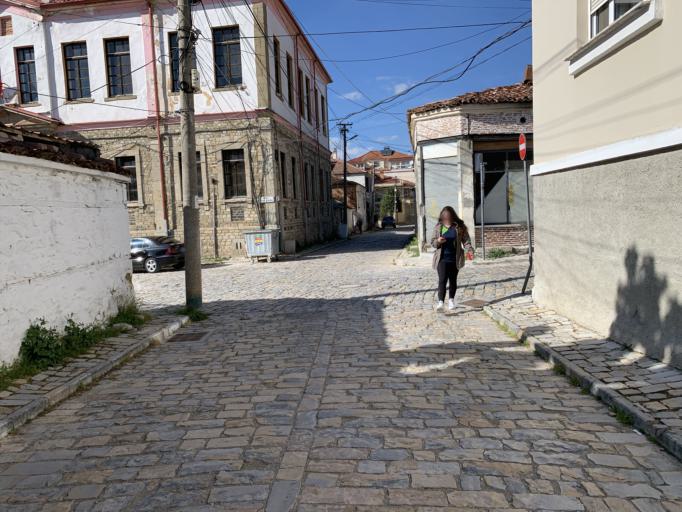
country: AL
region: Korce
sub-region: Rrethi i Korces
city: Korce
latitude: 40.6168
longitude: 20.7834
